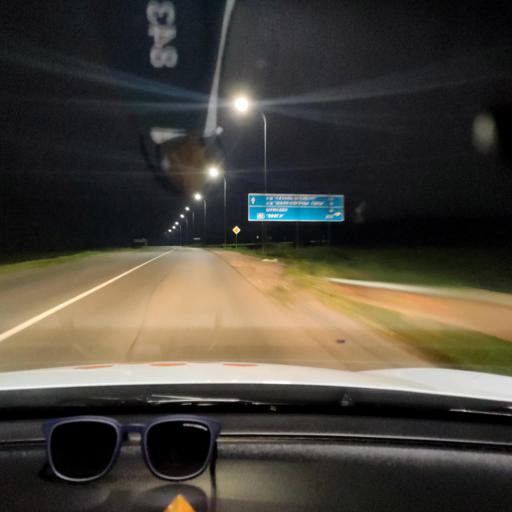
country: RU
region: Tatarstan
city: Rybnaya Sloboda
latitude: 55.4824
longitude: 50.1233
